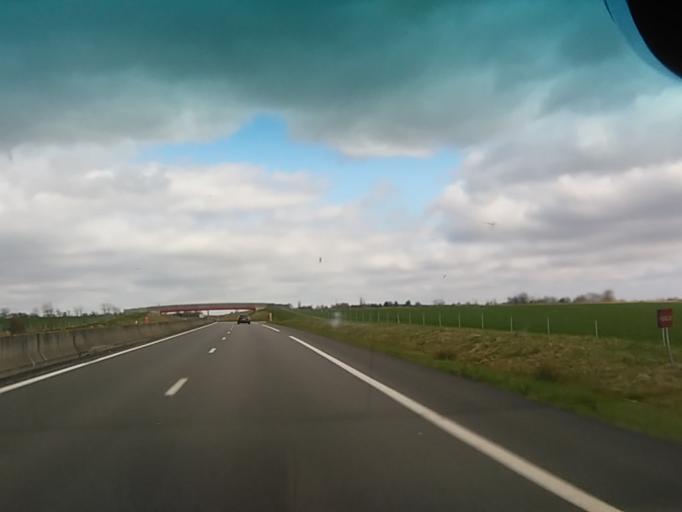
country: FR
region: Haute-Normandie
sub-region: Departement de l'Eure
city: Thiberville
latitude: 49.0998
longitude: 0.5044
